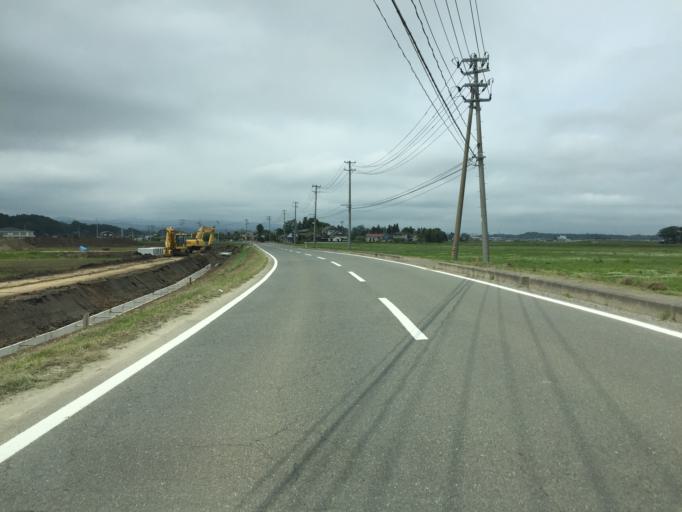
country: JP
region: Fukushima
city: Namie
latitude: 37.6876
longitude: 140.9883
